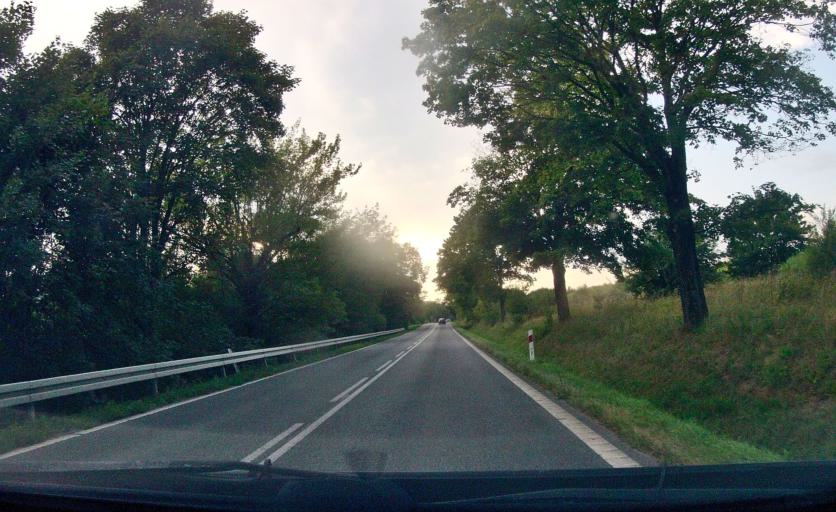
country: PL
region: Subcarpathian Voivodeship
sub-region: Powiat jasielski
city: Nowy Zmigrod
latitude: 49.5645
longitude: 21.5926
